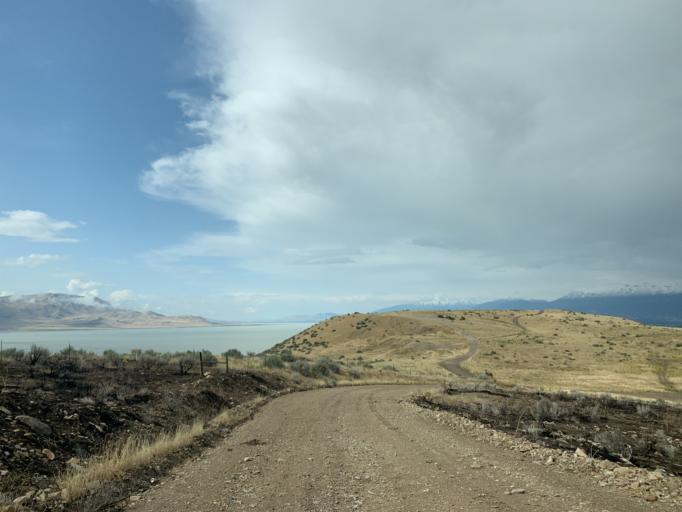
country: US
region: Utah
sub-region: Utah County
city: West Mountain
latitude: 40.1211
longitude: -111.8165
